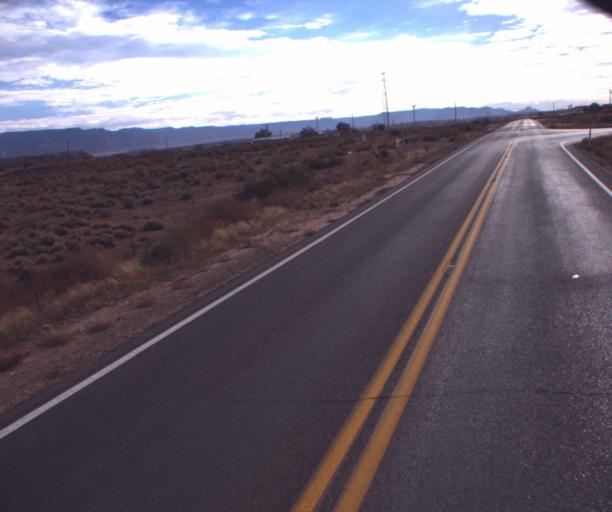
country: US
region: Arizona
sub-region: Apache County
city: Many Farms
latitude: 36.5094
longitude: -109.4732
